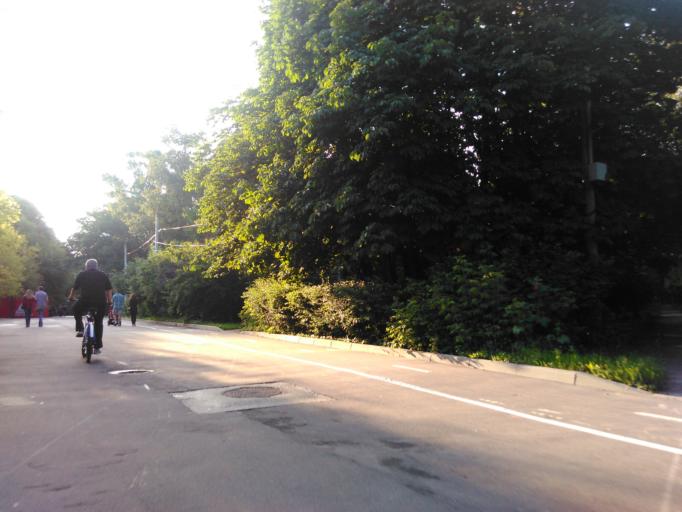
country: RU
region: Moscow
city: Sokol'niki
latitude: 55.7930
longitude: 37.6687
